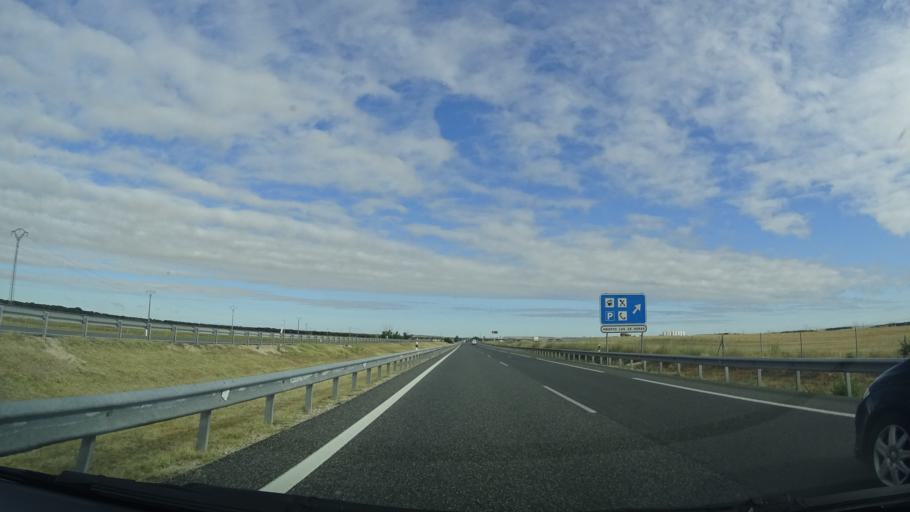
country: ES
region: Castille and Leon
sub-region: Provincia de Valladolid
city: Medina del Campo
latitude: 41.2663
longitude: -4.8819
